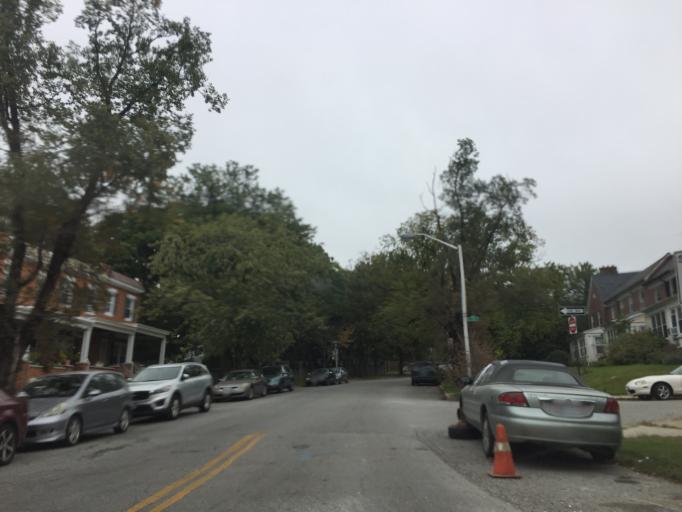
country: US
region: Maryland
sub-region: City of Baltimore
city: Baltimore
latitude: 39.3359
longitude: -76.6063
